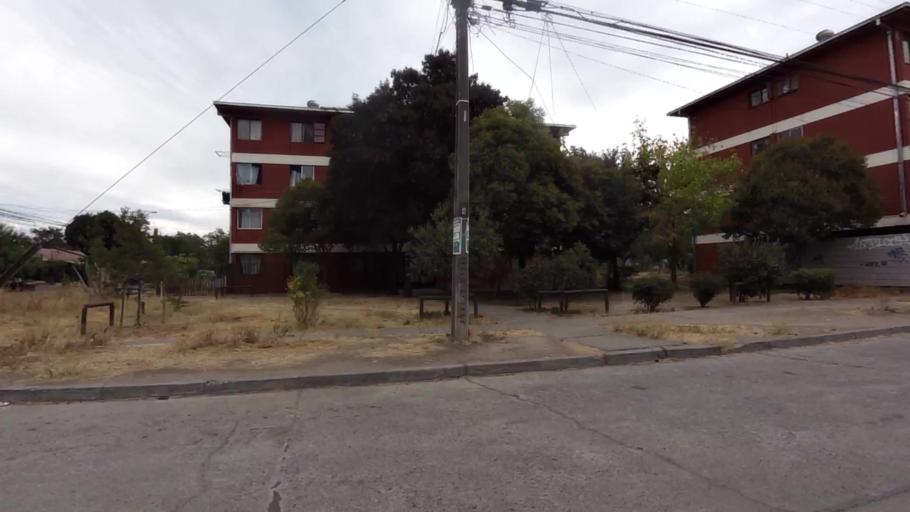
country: CL
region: O'Higgins
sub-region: Provincia de Cachapoal
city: Rancagua
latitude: -34.1526
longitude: -70.7417
